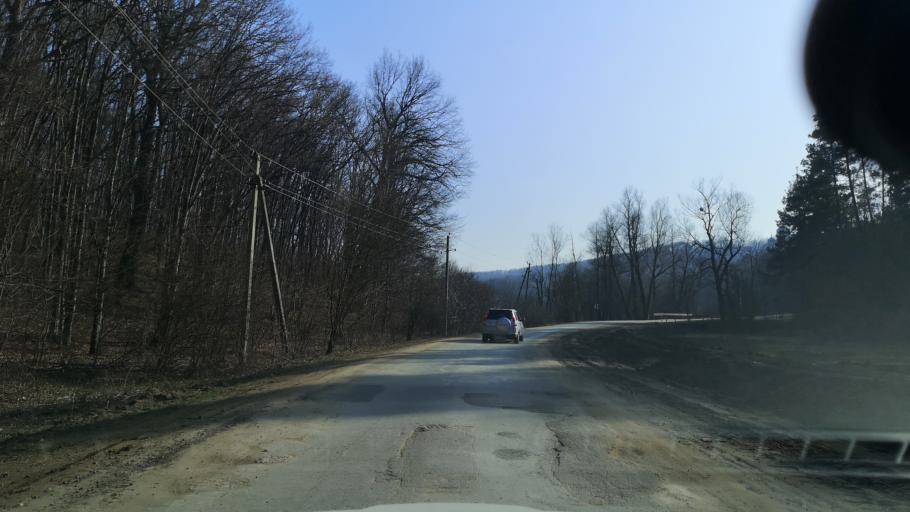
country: MD
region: Nisporeni
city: Nisporeni
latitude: 47.0848
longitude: 28.3217
